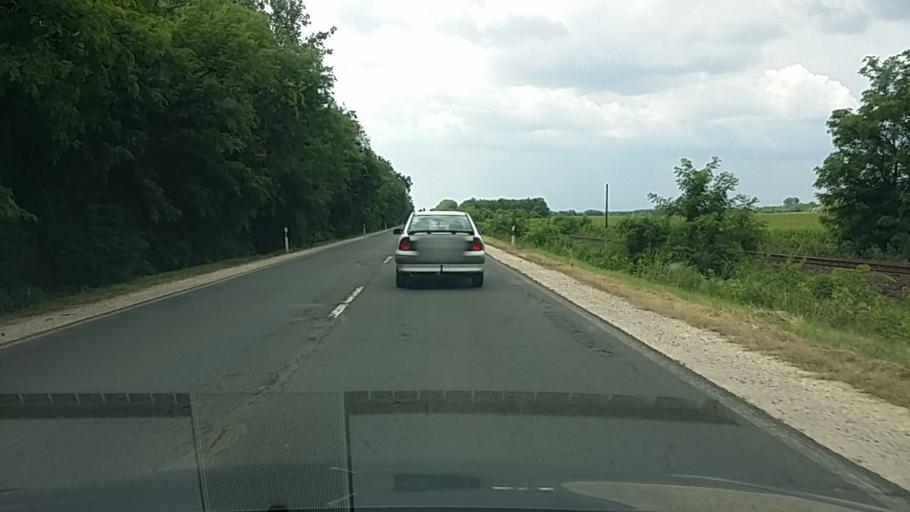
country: HU
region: Pest
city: Ujhartyan
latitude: 47.1670
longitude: 19.3745
